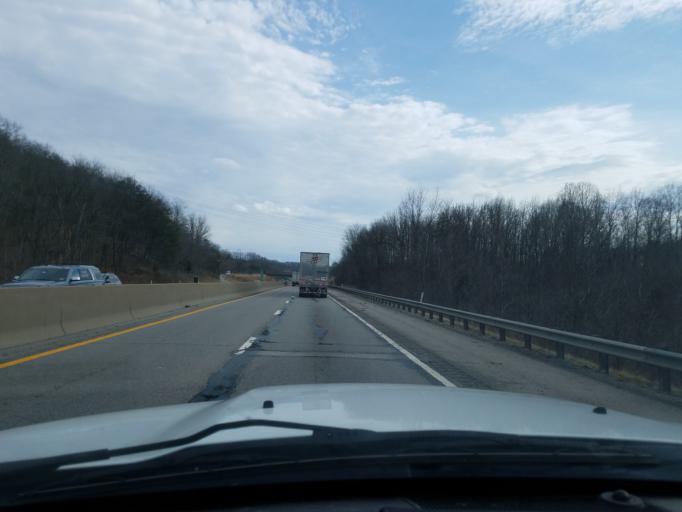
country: US
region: West Virginia
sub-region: Kanawha County
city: Nitro
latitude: 38.4503
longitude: -81.8538
